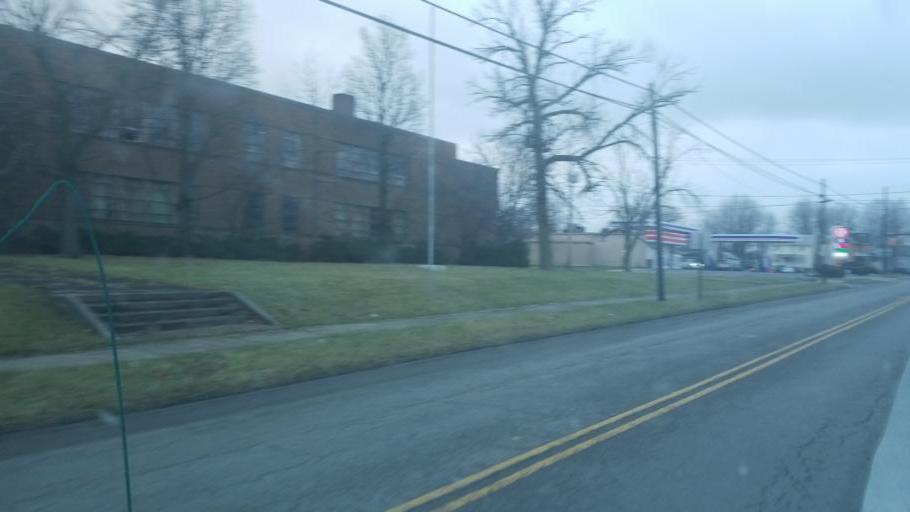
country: US
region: Ohio
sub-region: Crawford County
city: Galion
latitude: 40.7349
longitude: -82.7782
